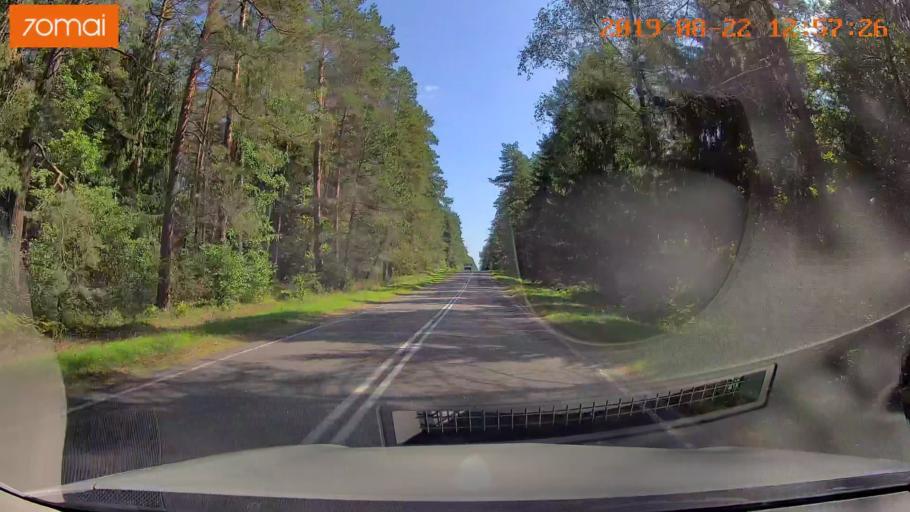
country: BY
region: Minsk
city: Prawdzinski
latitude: 53.4292
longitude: 27.7480
